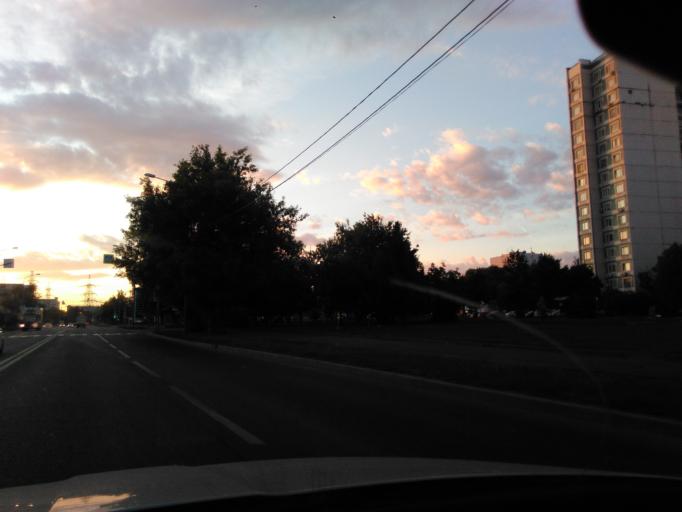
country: RU
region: Moscow
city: Businovo
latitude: 55.8857
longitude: 37.5153
